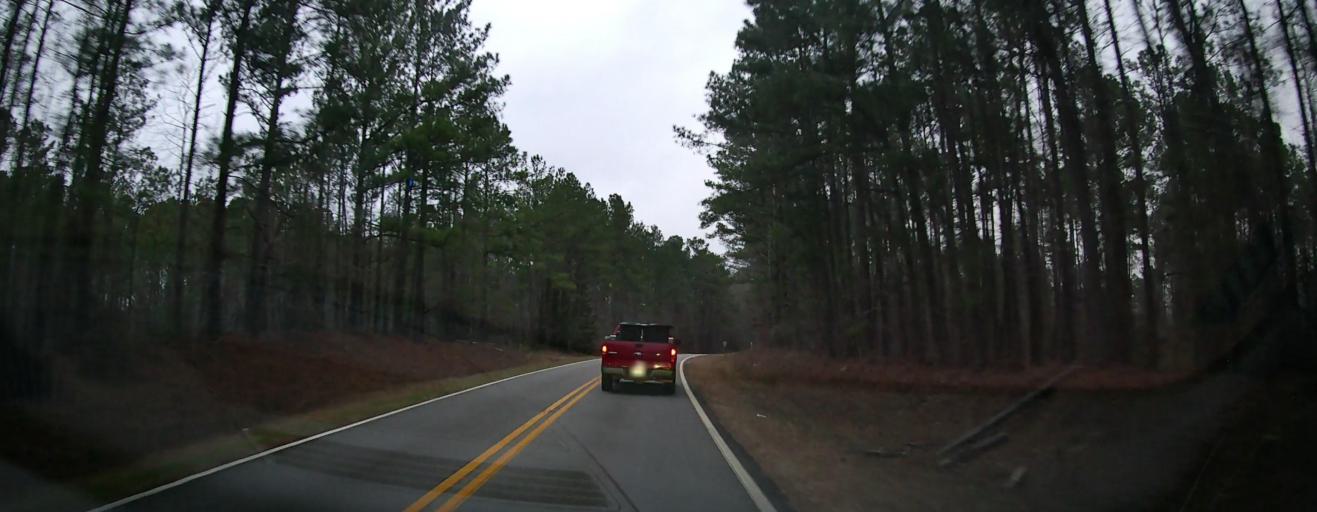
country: US
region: Georgia
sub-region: Monroe County
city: Forsyth
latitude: 32.9242
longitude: -83.8828
